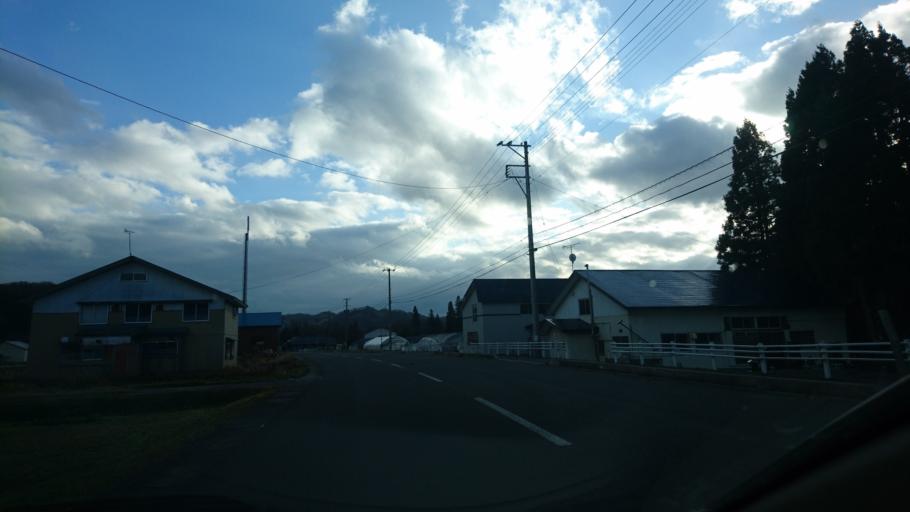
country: JP
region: Akita
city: Yokotemachi
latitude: 39.3601
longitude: 140.7701
